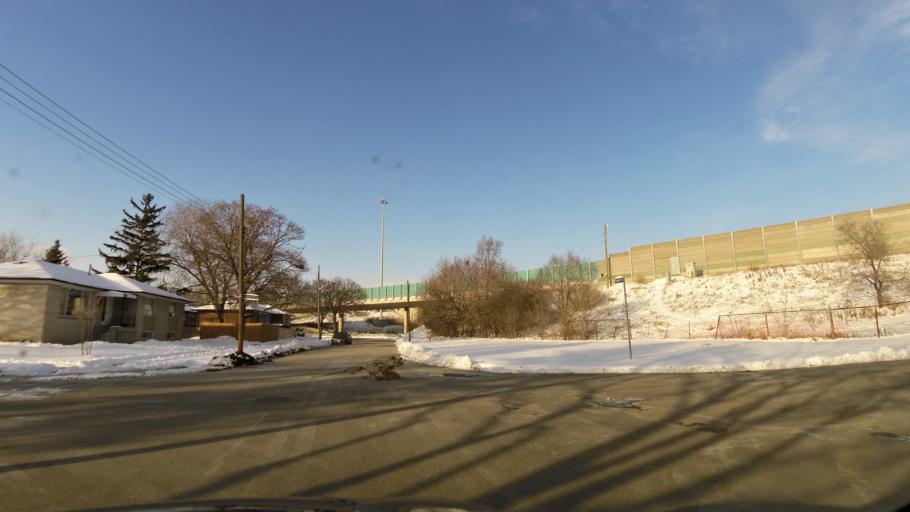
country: CA
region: Ontario
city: Etobicoke
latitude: 43.6696
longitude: -79.5763
